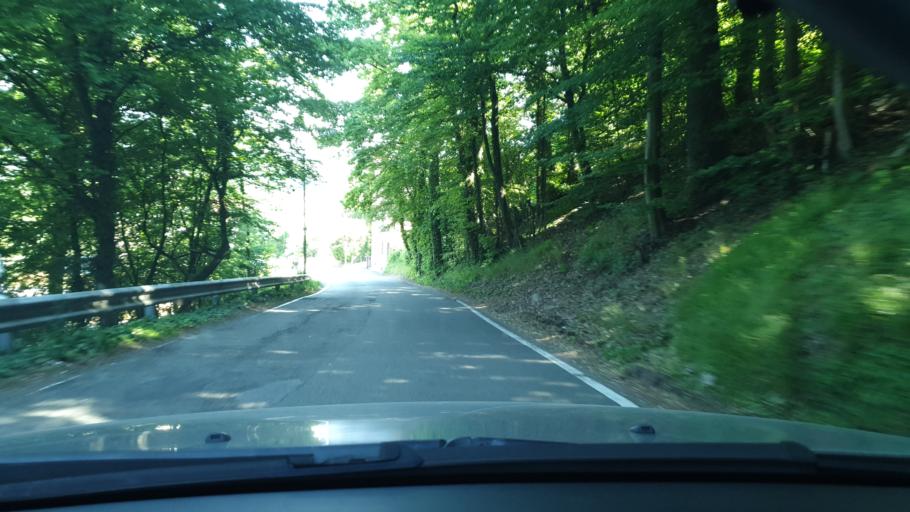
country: DE
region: Rheinland-Pfalz
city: Otterberg
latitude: 49.4755
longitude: 7.7875
